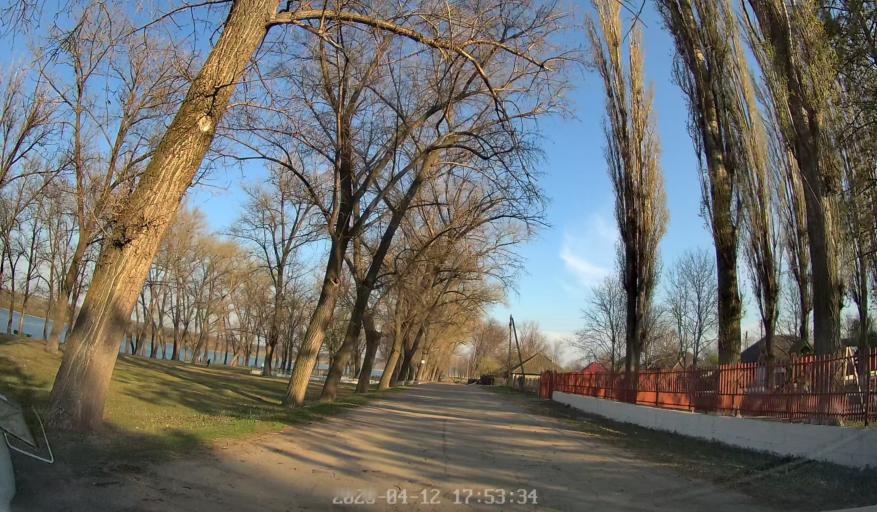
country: MD
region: Telenesti
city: Cocieri
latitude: 47.3831
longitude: 29.1241
